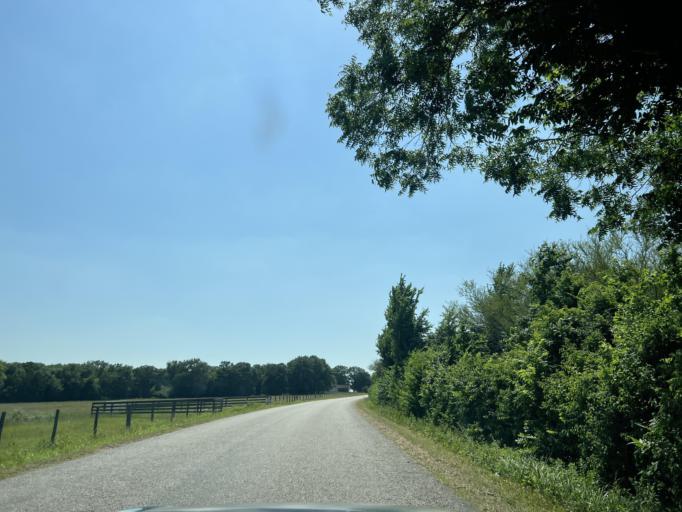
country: US
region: Texas
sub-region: Washington County
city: Brenham
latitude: 30.1534
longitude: -96.4755
